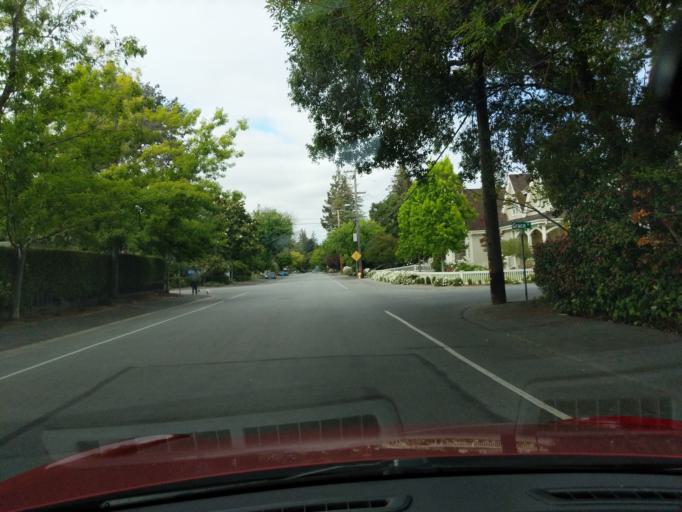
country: US
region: California
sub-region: San Mateo County
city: West Menlo Park
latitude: 37.4348
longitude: -122.1918
